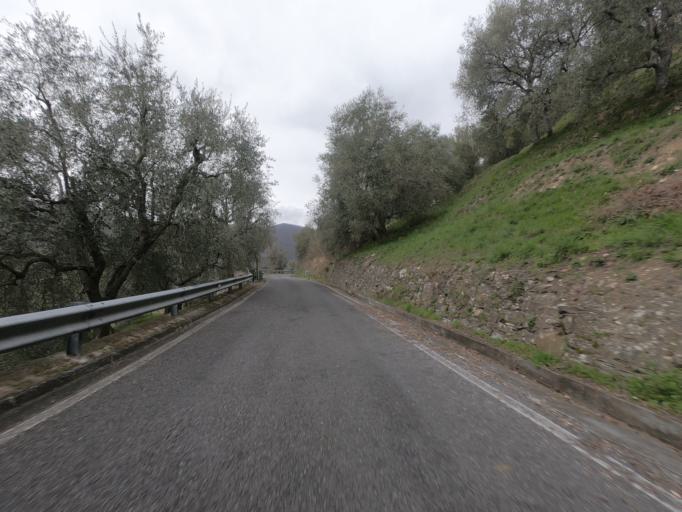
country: IT
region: Liguria
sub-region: Provincia di Savona
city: Testico
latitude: 44.0249
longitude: 8.0065
